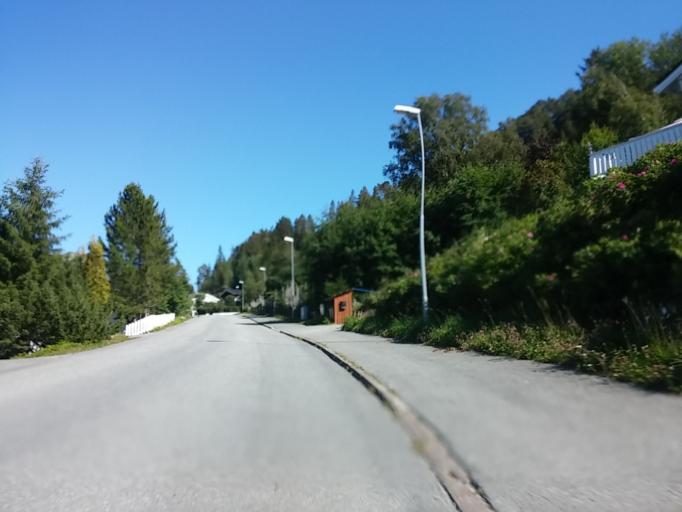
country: NO
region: Sor-Trondelag
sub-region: Malvik
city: Hommelvik
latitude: 63.4299
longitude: 10.7476
